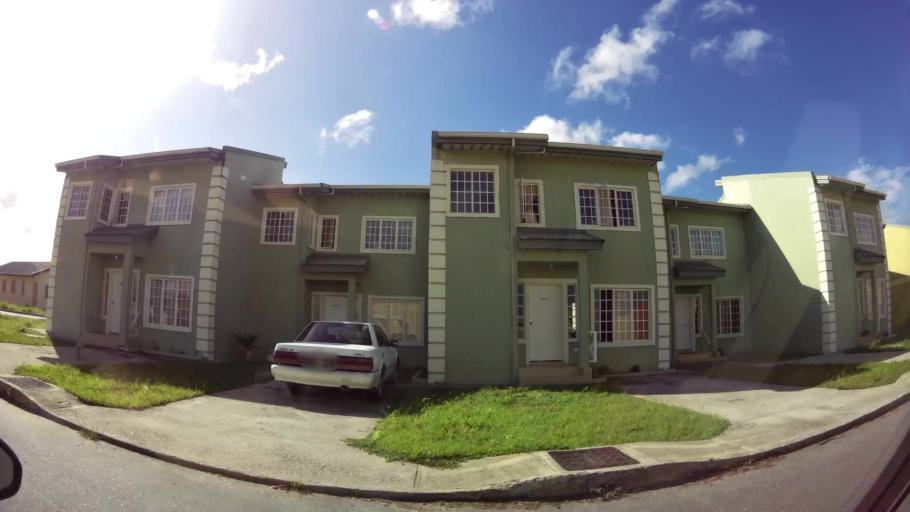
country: TT
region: Chaguanas
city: Chaguanas
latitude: 10.5322
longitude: -61.3941
